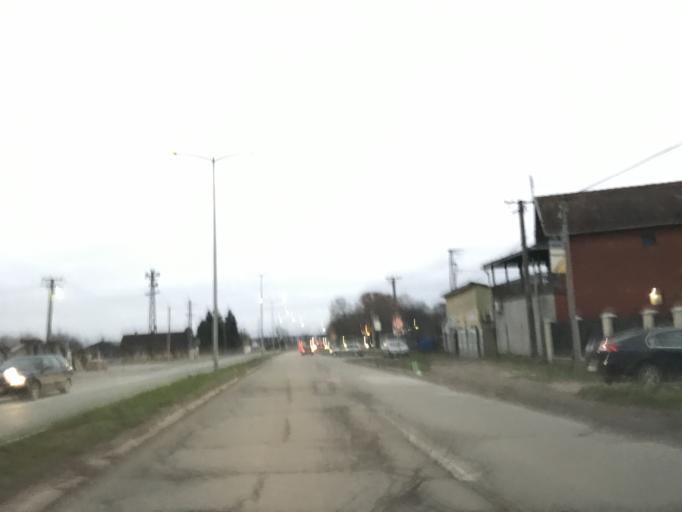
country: RS
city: Veternik
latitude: 45.2794
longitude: 19.7905
